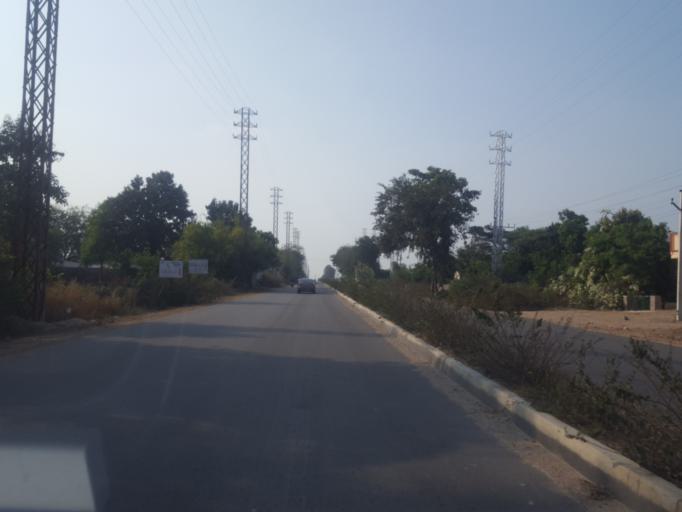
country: IN
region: Telangana
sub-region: Medak
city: Serilingampalle
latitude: 17.4132
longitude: 78.2656
